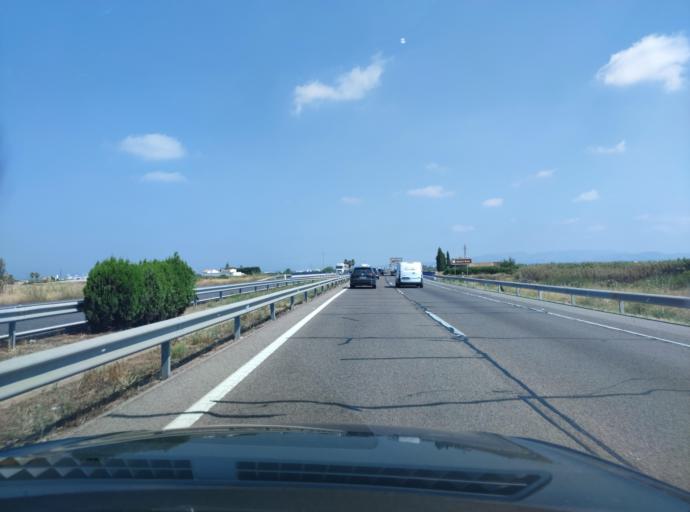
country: ES
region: Valencia
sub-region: Provincia de Castello
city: Alquerias del Nino Perdido
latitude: 39.9084
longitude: -0.1351
